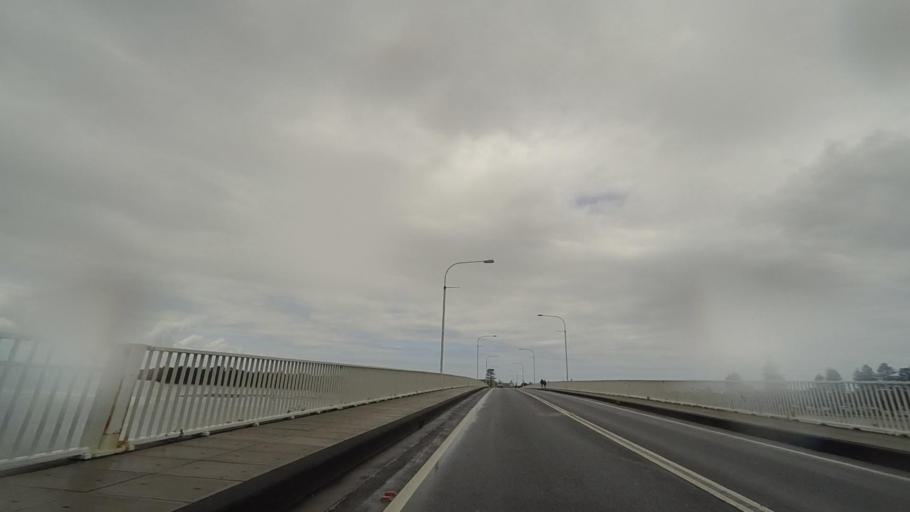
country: AU
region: New South Wales
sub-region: Wyong Shire
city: The Entrance
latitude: -33.3387
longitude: 151.4988
